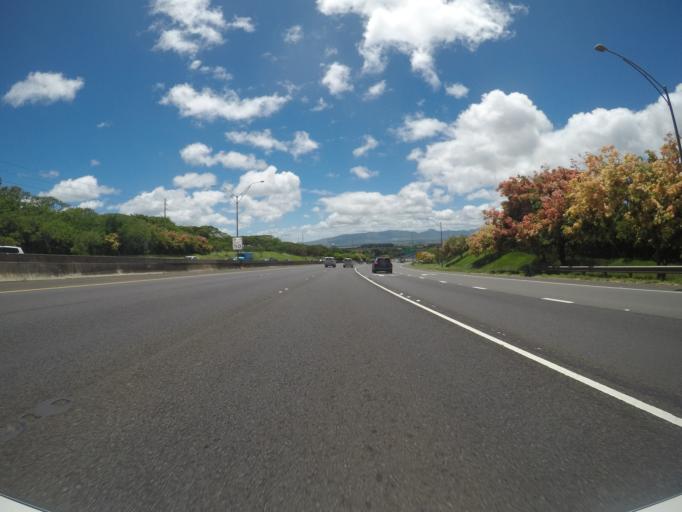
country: US
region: Hawaii
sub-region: Honolulu County
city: Halawa Heights
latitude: 21.3687
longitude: -157.9091
